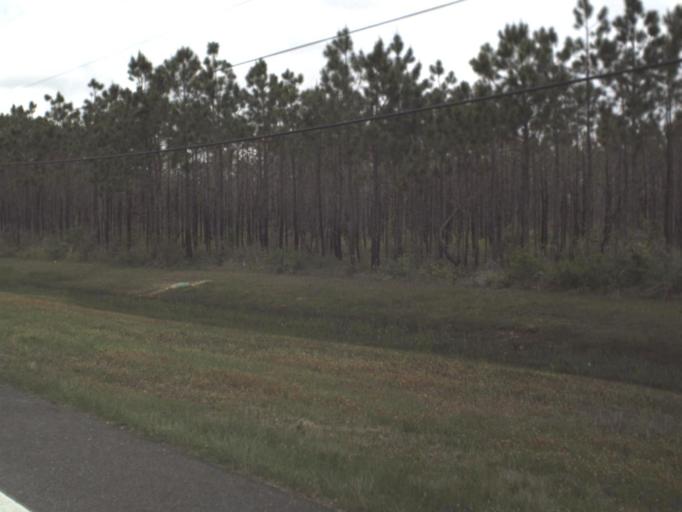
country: US
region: Florida
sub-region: Santa Rosa County
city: Bagdad
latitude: 30.5180
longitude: -87.0873
